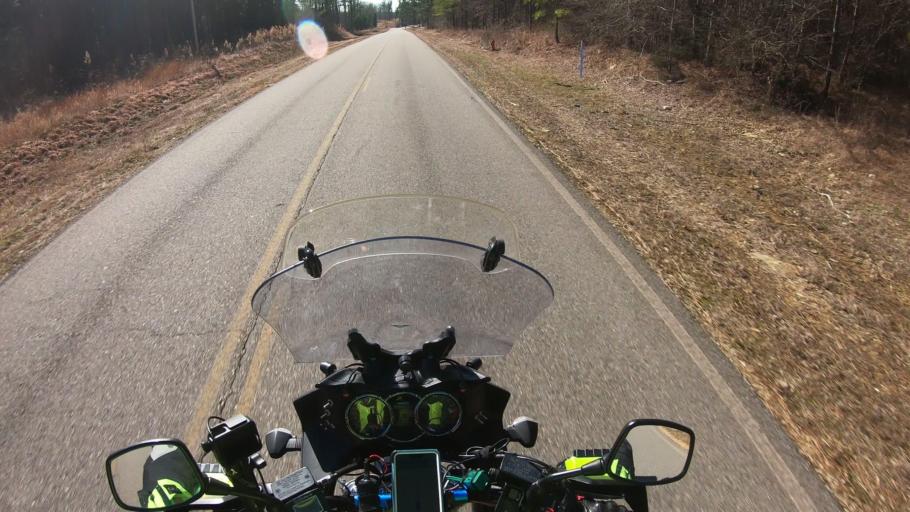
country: US
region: Alabama
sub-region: Clay County
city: Lineville
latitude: 33.3980
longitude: -85.8076
